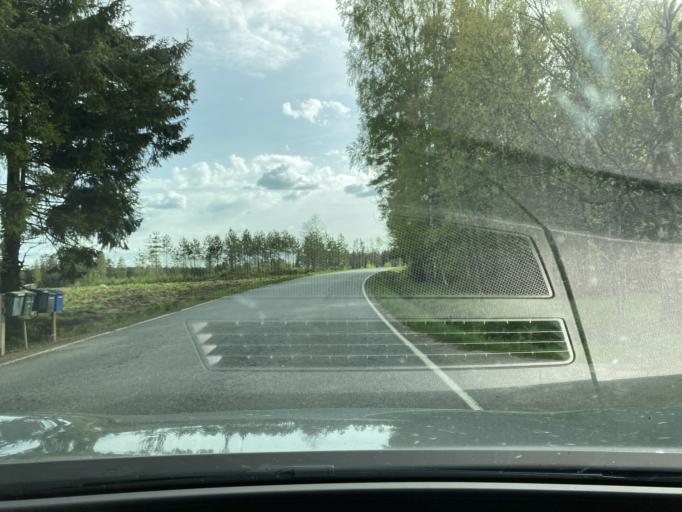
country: FI
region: Varsinais-Suomi
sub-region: Salo
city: Kiikala
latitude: 60.5209
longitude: 23.5411
